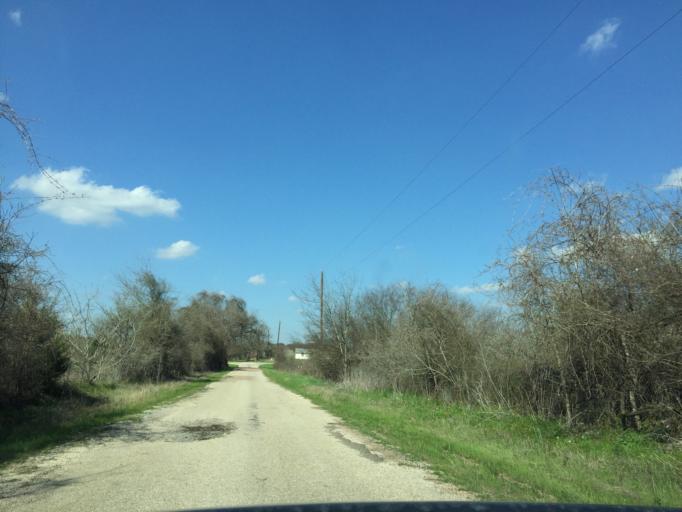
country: US
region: Texas
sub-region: Milam County
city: Thorndale
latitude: 30.5587
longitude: -97.1442
